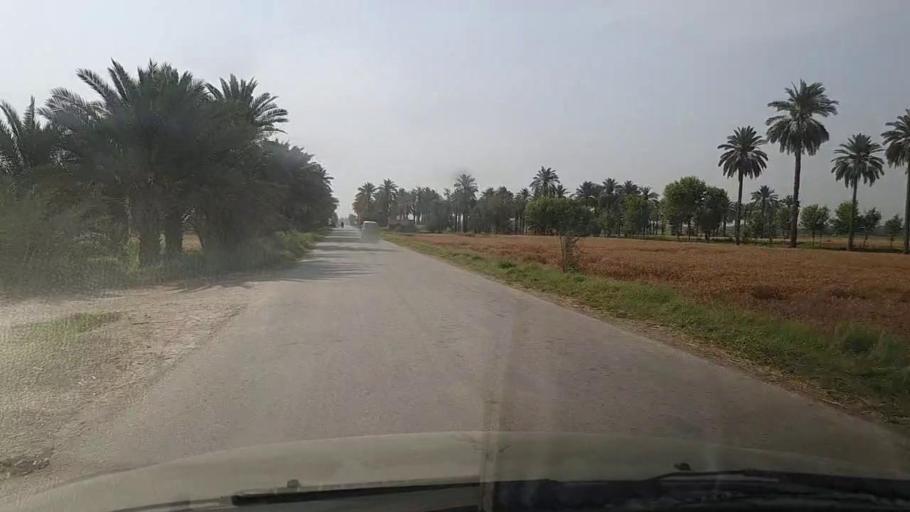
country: PK
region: Sindh
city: Gambat
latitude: 27.4684
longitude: 68.4768
